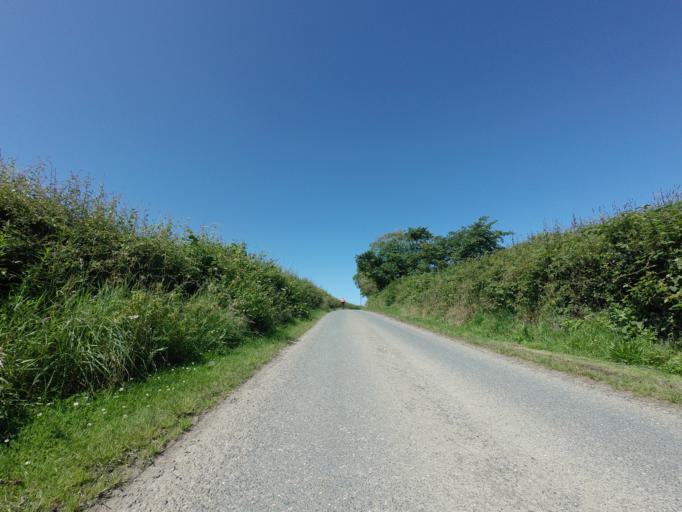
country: GB
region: Scotland
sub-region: Aberdeenshire
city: Macduff
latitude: 57.6332
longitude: -2.4889
